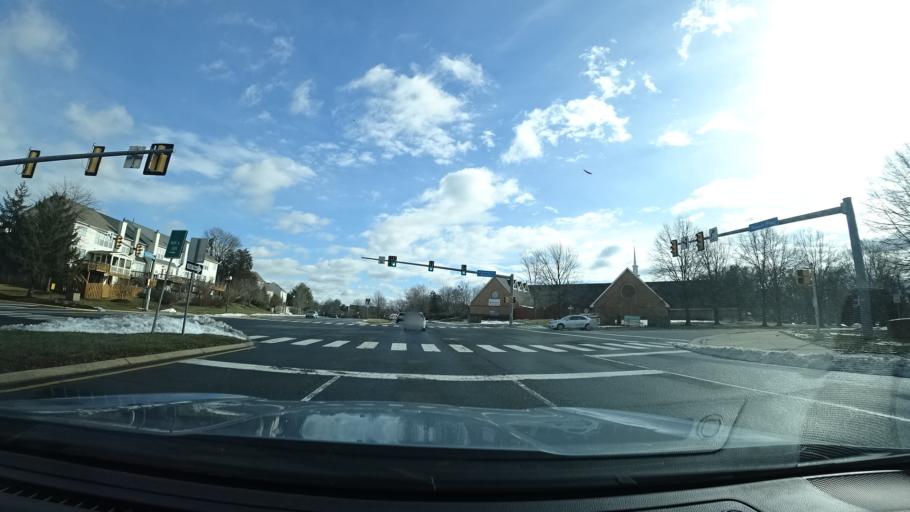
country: US
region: Virginia
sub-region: Loudoun County
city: Countryside
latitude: 39.0353
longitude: -77.3951
